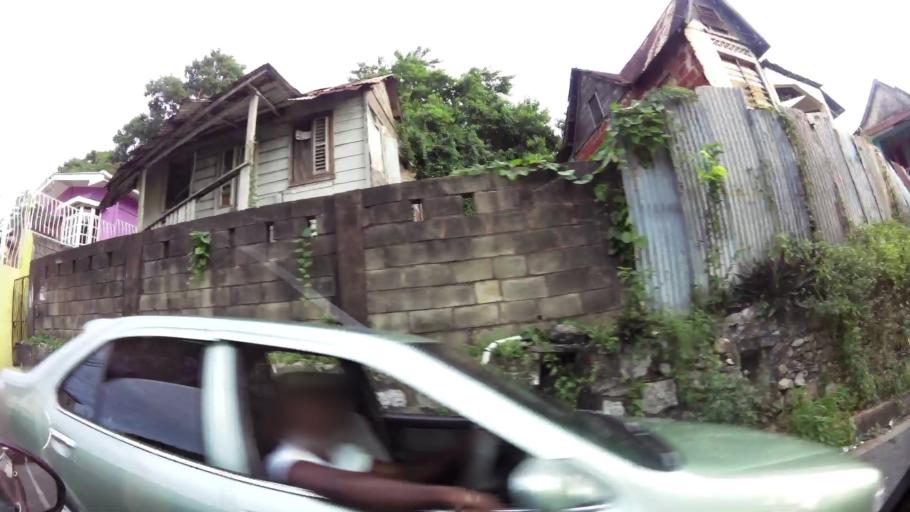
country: TT
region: San Juan/Laventille
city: Laventille
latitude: 10.6558
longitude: -61.5032
